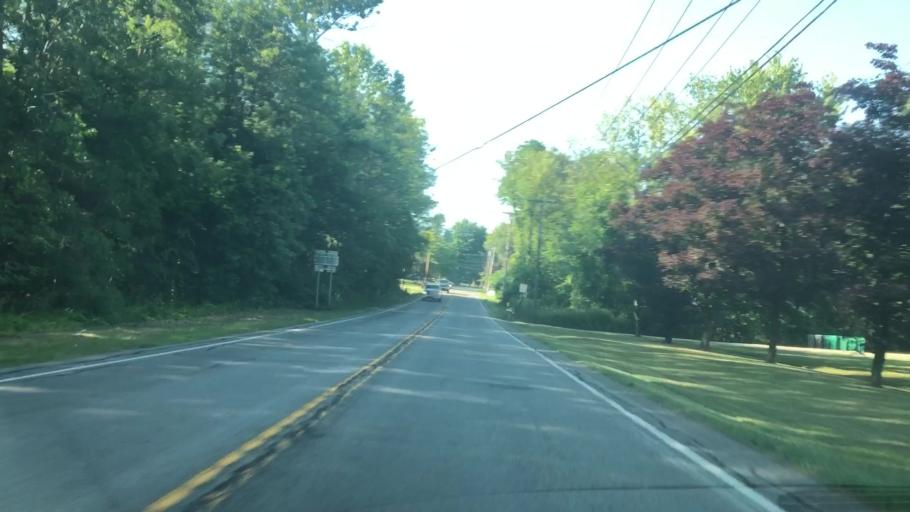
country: US
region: New York
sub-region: Wayne County
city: Ontario
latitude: 43.1648
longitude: -77.2898
